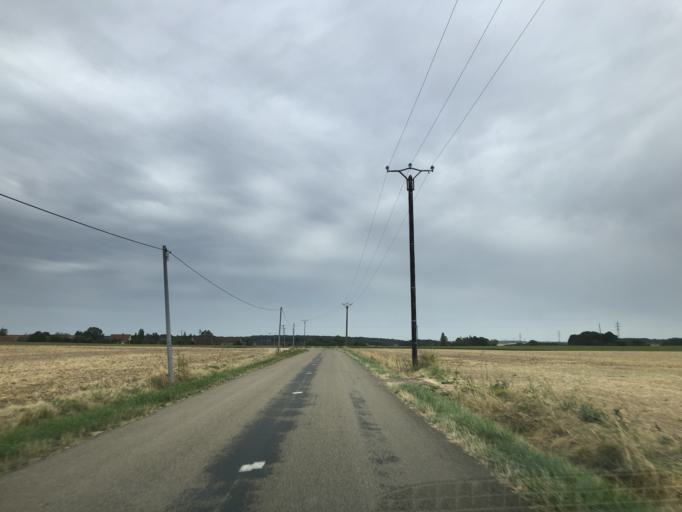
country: FR
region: Centre
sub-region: Departement du Loiret
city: Douchy
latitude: 47.9795
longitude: 3.1422
